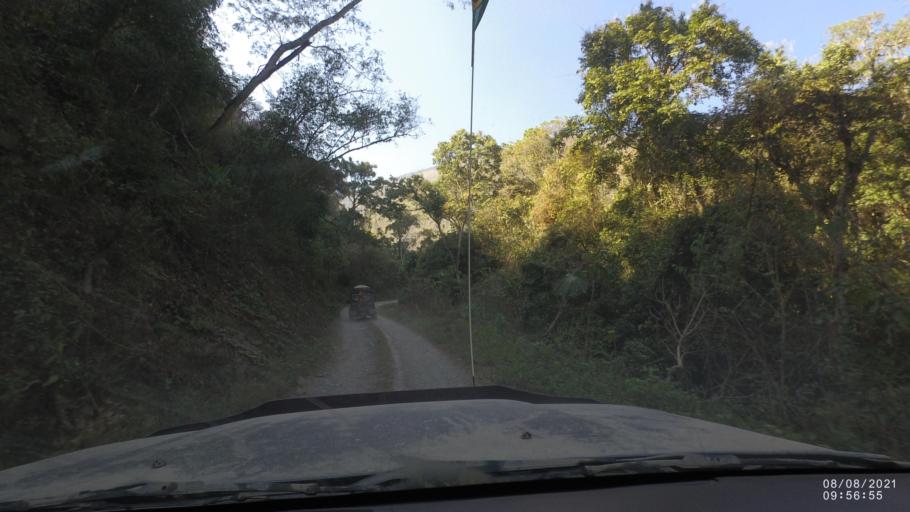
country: BO
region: La Paz
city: Quime
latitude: -16.6395
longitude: -66.7250
